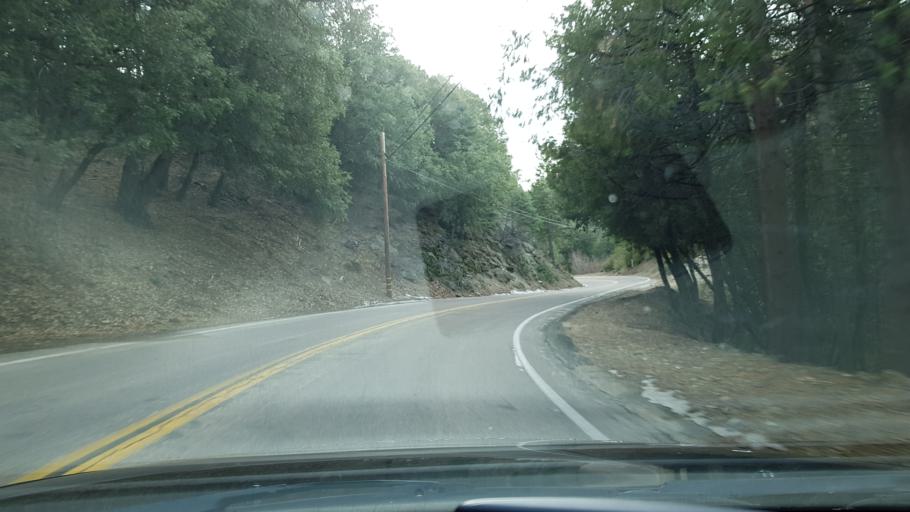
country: US
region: California
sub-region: Riverside County
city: Aguanga
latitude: 33.3537
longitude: -116.8701
